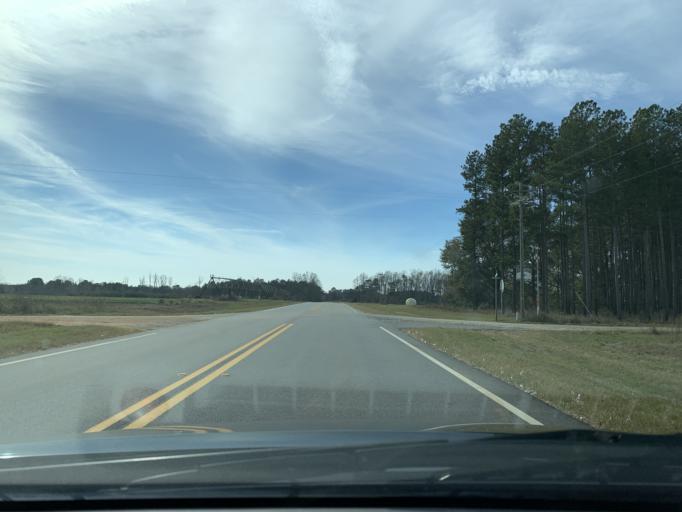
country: US
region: Georgia
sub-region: Turner County
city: Ashburn
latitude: 31.7480
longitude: -83.5628
